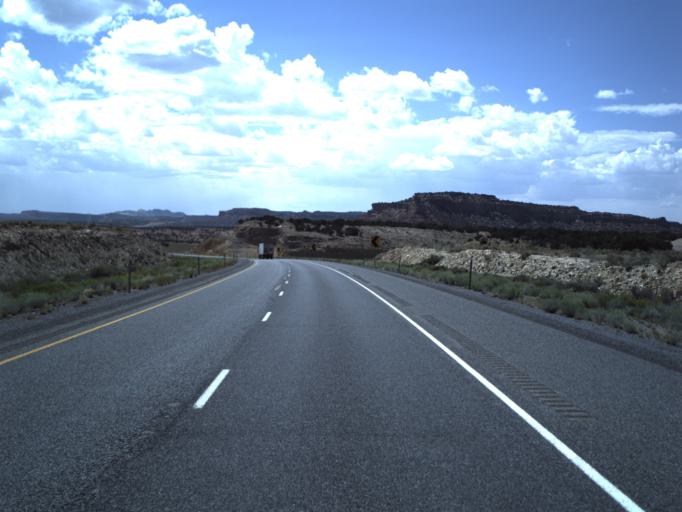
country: US
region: Utah
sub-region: Emery County
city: Castle Dale
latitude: 38.8912
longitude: -110.6411
